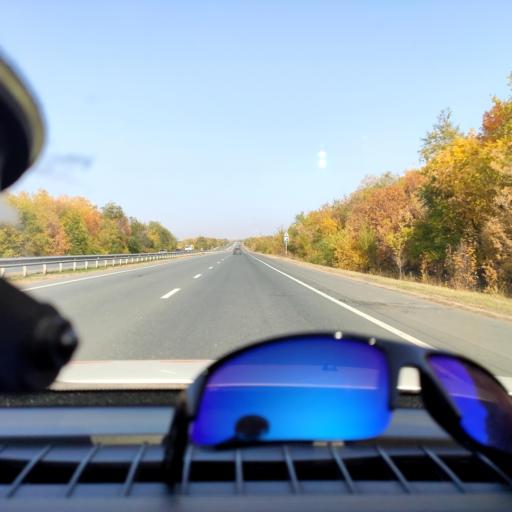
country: RU
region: Samara
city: Novokuybyshevsk
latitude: 53.0354
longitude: 49.9984
